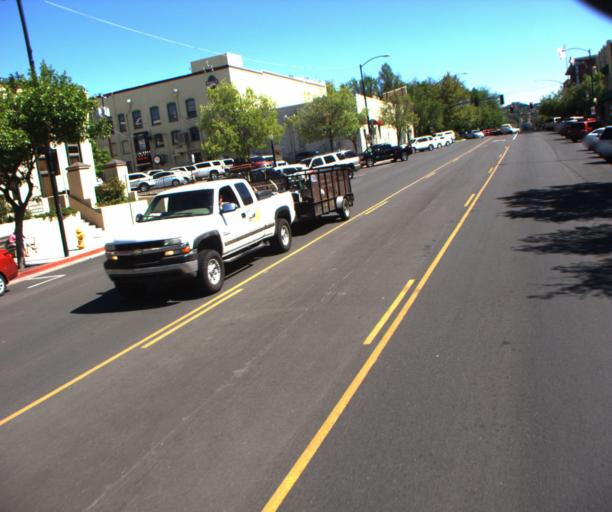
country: US
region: Arizona
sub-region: Yavapai County
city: Prescott
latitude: 34.5430
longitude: -112.4701
